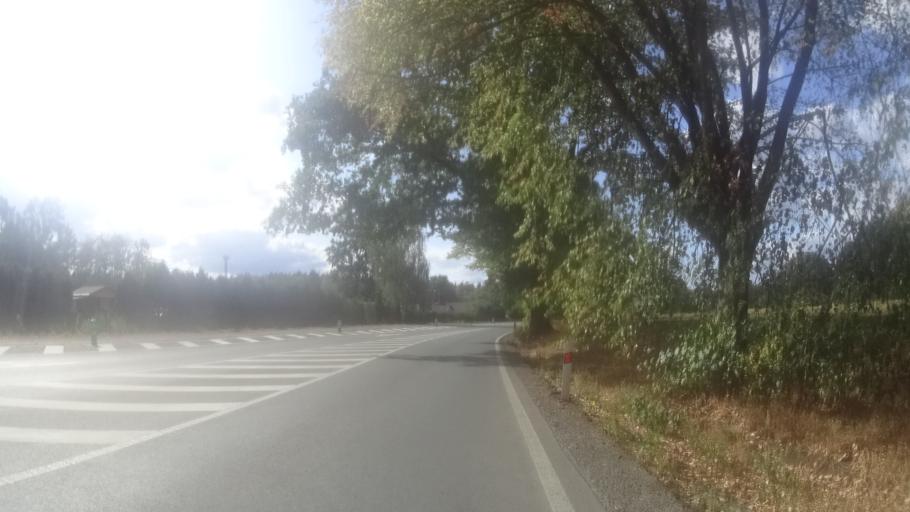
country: CZ
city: Borohradek
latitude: 50.1039
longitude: 16.0831
